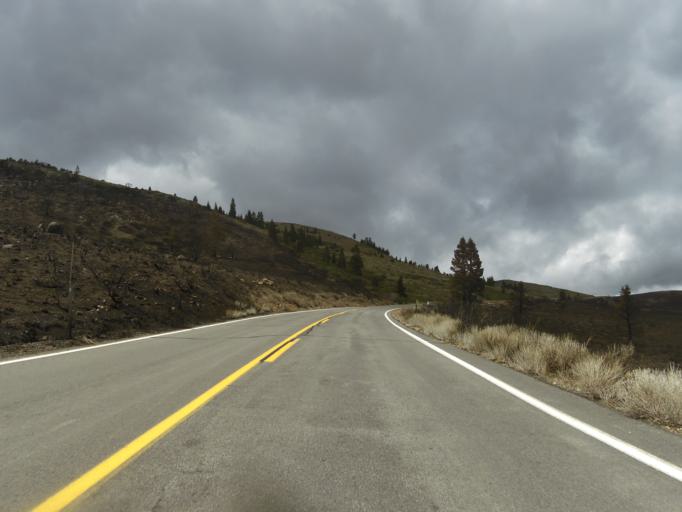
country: US
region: Nevada
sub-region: Douglas County
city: Gardnerville Ranchos
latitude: 38.6716
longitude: -119.5865
